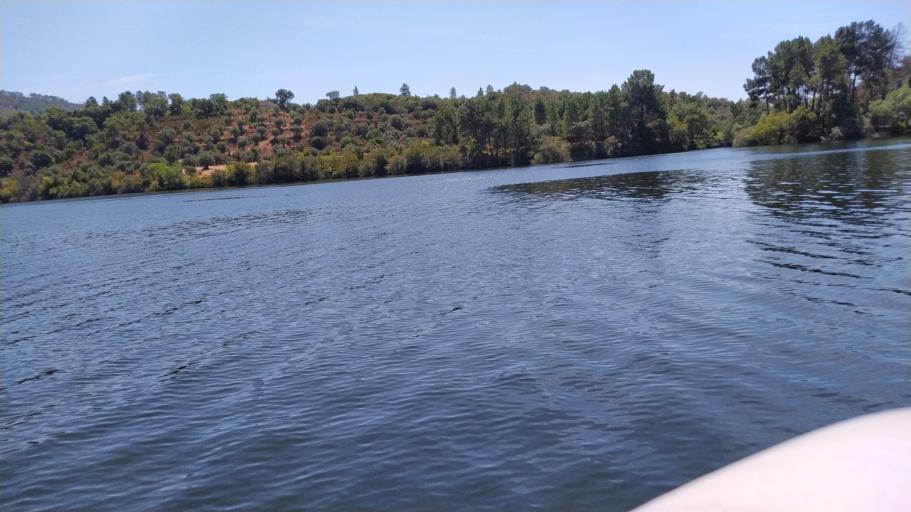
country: PT
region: Portalegre
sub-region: Nisa
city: Nisa
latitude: 39.6387
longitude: -7.6980
